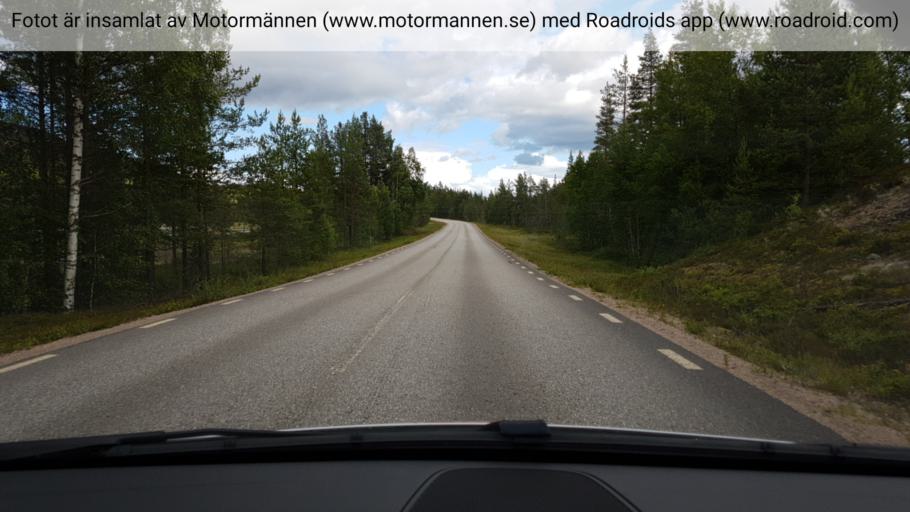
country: SE
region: Jaemtland
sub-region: Harjedalens Kommun
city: Sveg
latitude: 62.0018
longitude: 14.9162
